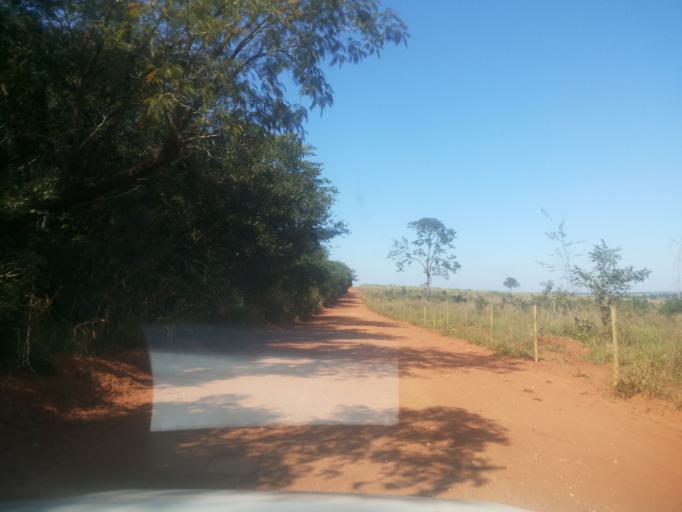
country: BR
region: Minas Gerais
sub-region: Santa Vitoria
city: Santa Vitoria
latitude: -19.0115
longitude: -50.3719
